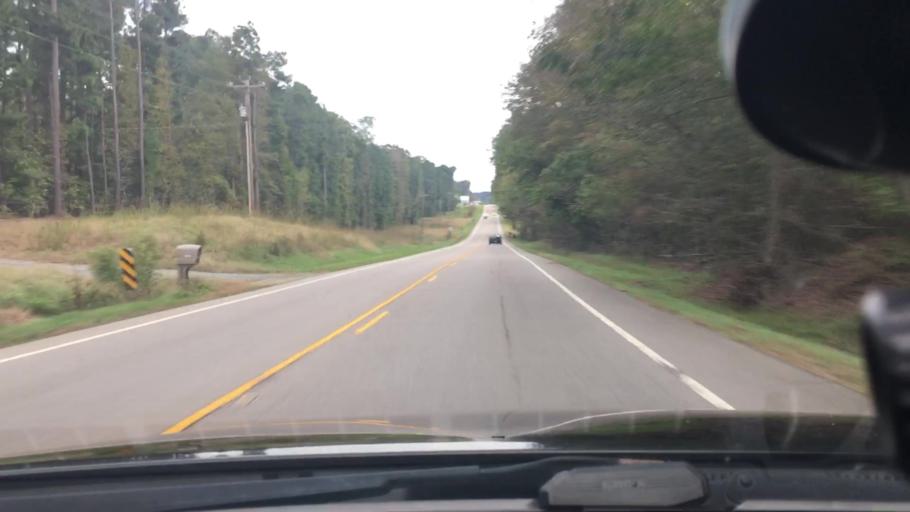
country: US
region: North Carolina
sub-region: Moore County
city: Robbins
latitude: 35.3879
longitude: -79.5035
